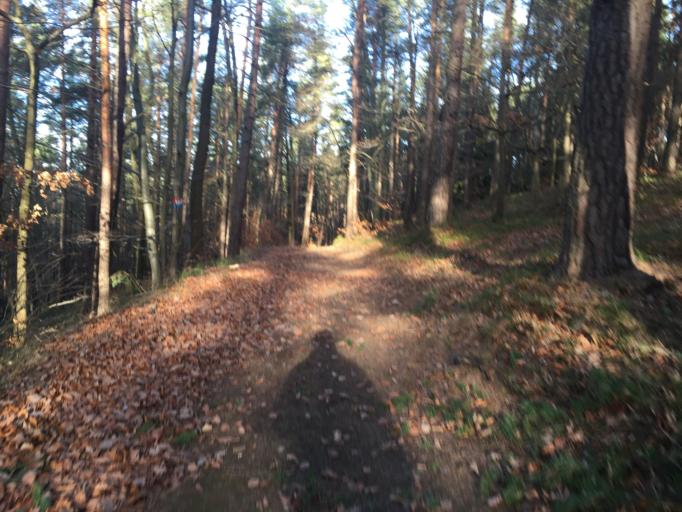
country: DE
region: Thuringia
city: Bad Blankenburg
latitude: 50.6561
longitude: 11.2706
